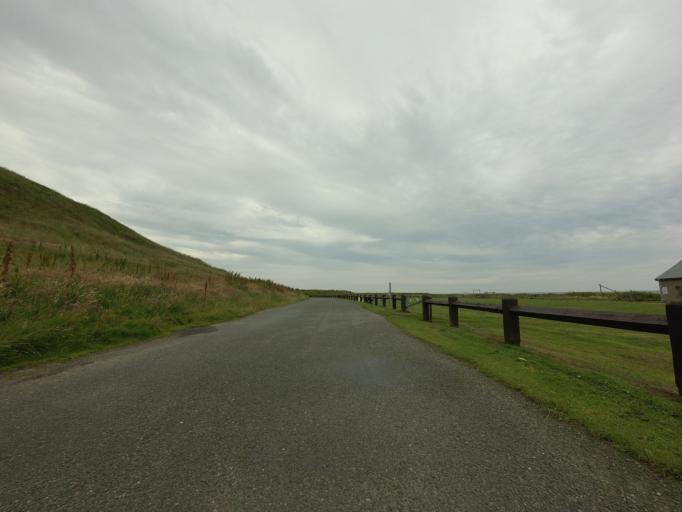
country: GB
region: Scotland
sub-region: Aberdeenshire
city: Whitehills
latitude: 57.6811
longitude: -2.5737
